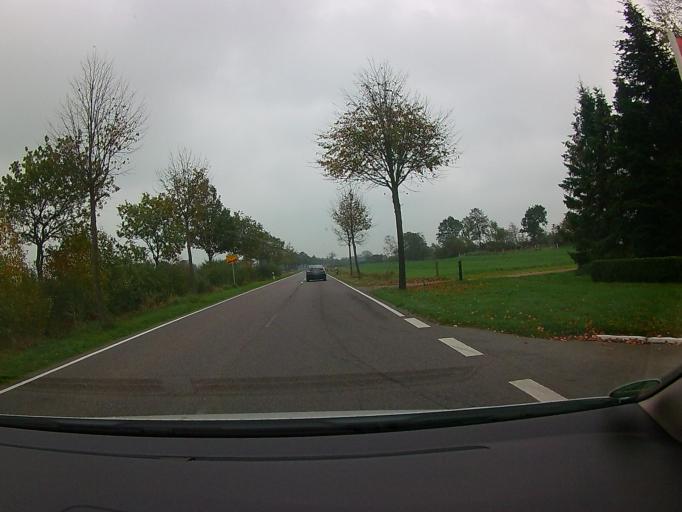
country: DE
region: Schleswig-Holstein
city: Goldelund
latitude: 54.6783
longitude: 9.1127
